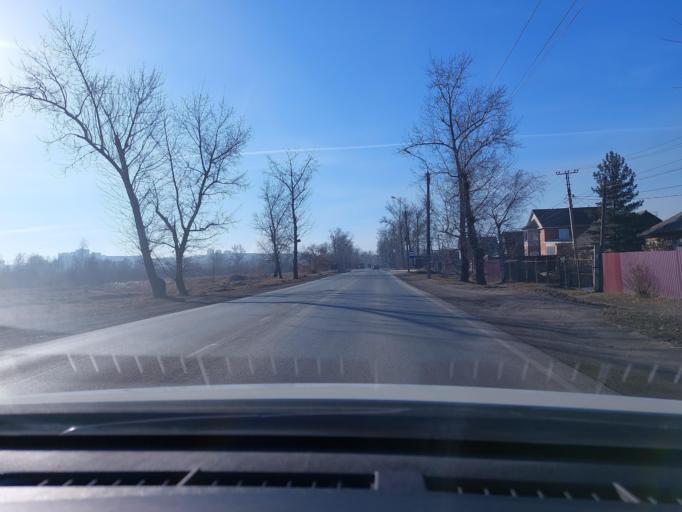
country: RU
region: Irkutsk
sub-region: Irkutskiy Rayon
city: Irkutsk
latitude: 52.3052
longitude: 104.2535
